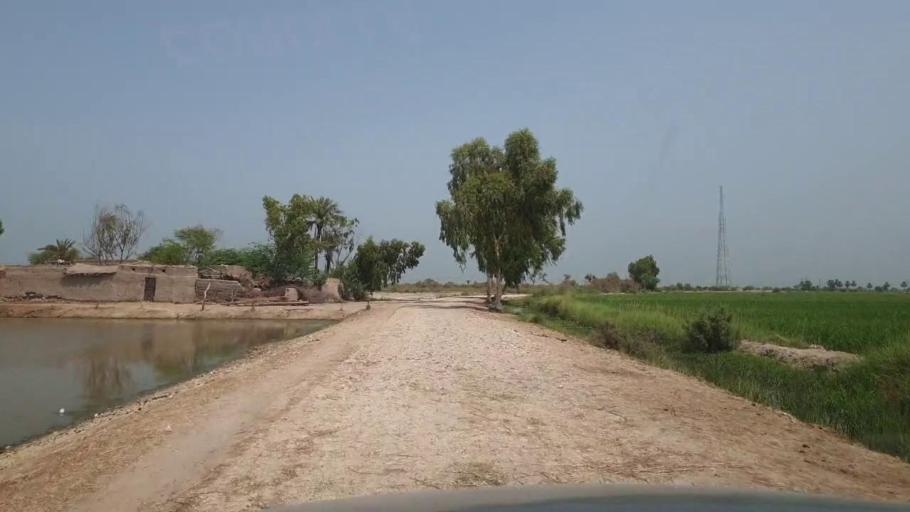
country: PK
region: Sindh
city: Madeji
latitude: 27.8005
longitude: 68.5318
